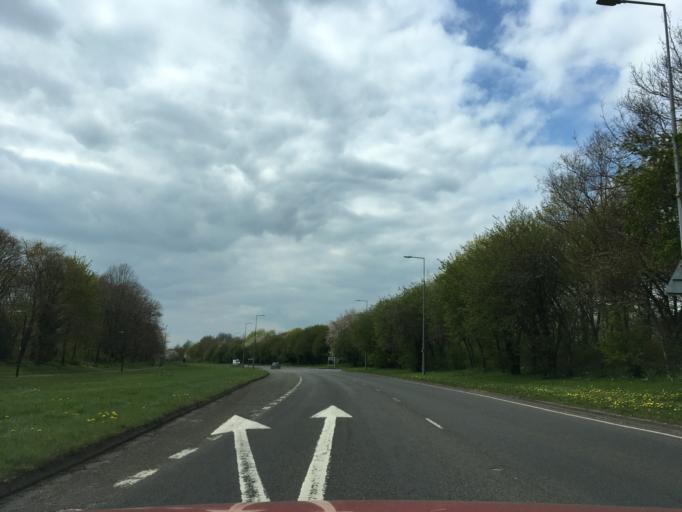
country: GB
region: England
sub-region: Milton Keynes
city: Milton Keynes
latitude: 52.0684
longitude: -0.7648
